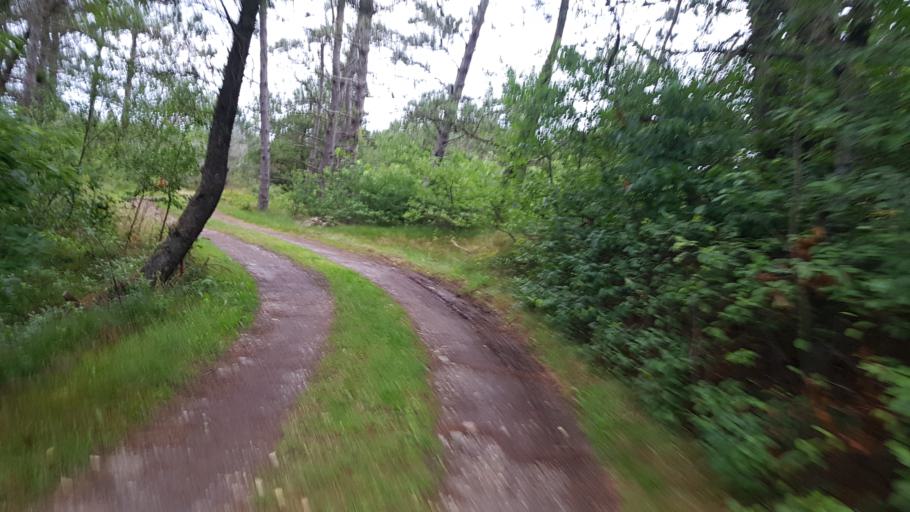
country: DE
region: Schleswig-Holstein
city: List
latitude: 55.0972
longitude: 8.5388
